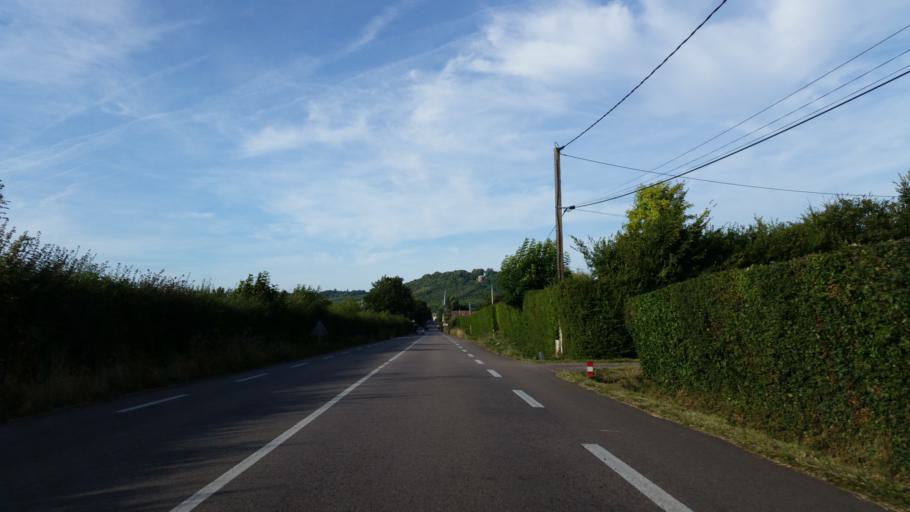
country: FR
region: Lower Normandy
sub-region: Departement du Calvados
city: Cambremer
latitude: 49.1111
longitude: 0.0083
